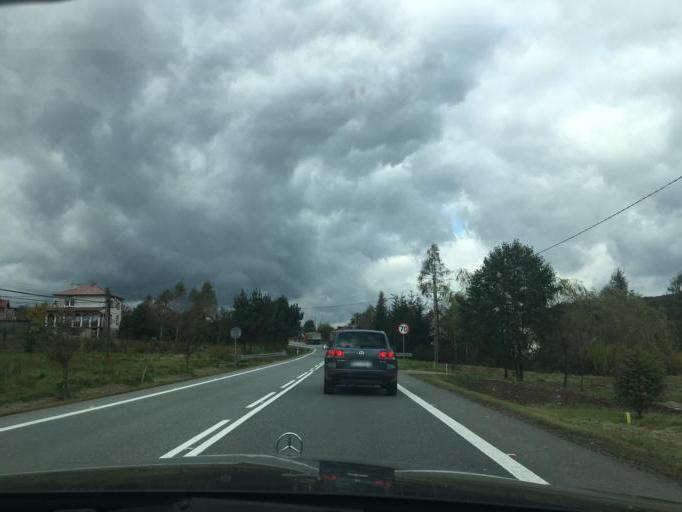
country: PL
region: Subcarpathian Voivodeship
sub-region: Powiat strzyzowski
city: Polomia
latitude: 49.8954
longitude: 21.8887
